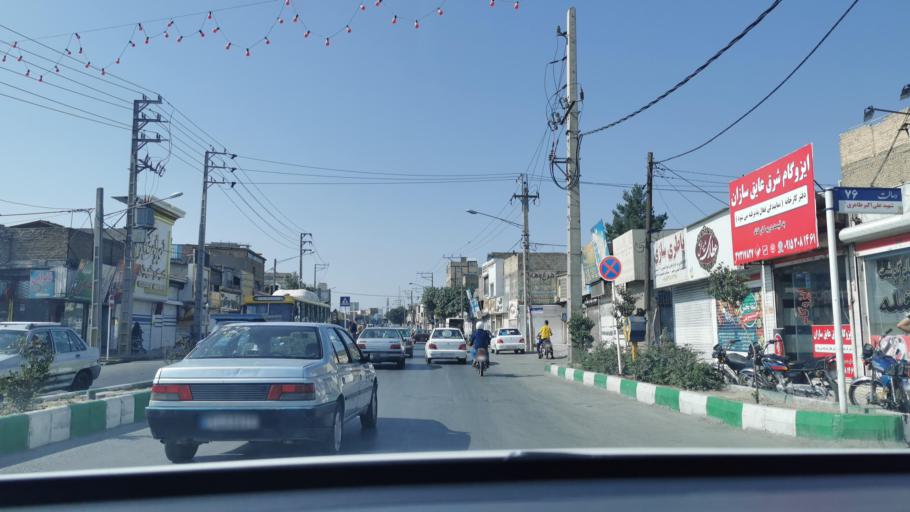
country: IR
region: Razavi Khorasan
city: Mashhad
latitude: 36.3258
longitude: 59.6422
